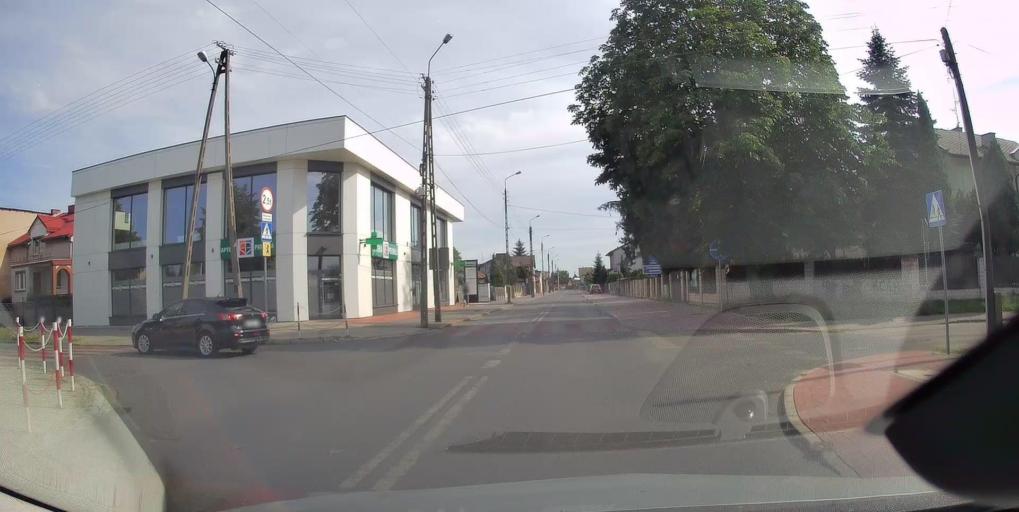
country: PL
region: Lodz Voivodeship
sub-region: Powiat tomaszowski
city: Tomaszow Mazowiecki
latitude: 51.5275
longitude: 19.9973
